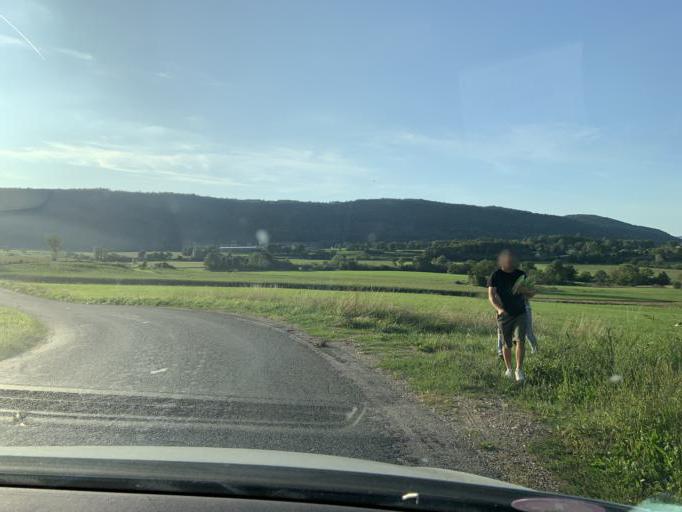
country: FR
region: Rhone-Alpes
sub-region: Departement de l'Ain
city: Dortan
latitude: 46.2948
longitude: 5.6469
